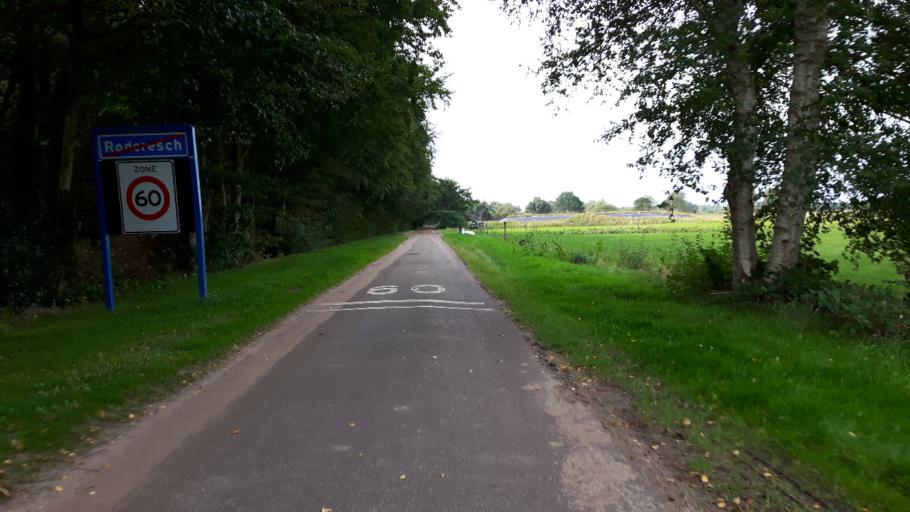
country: NL
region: Groningen
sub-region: Gemeente Leek
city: Leek
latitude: 53.1114
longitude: 6.4154
